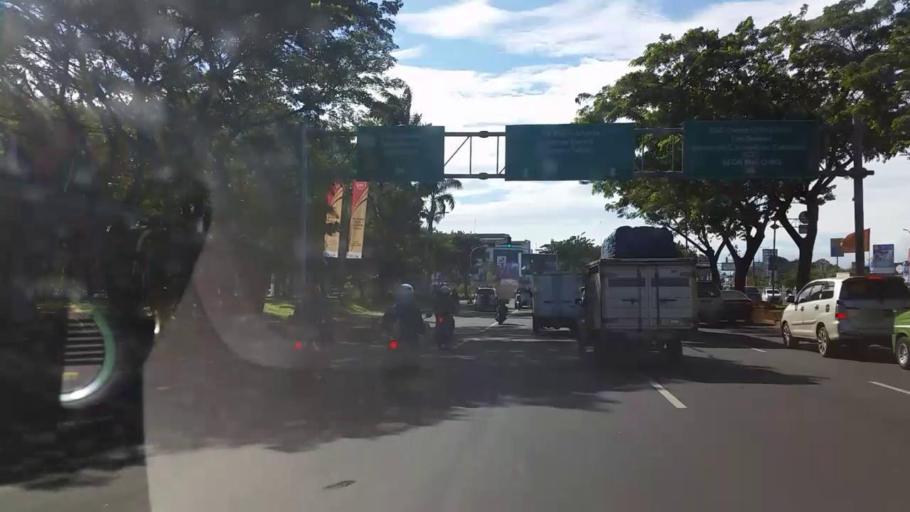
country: ID
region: West Java
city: Serpong
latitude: -6.2985
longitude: 106.6675
